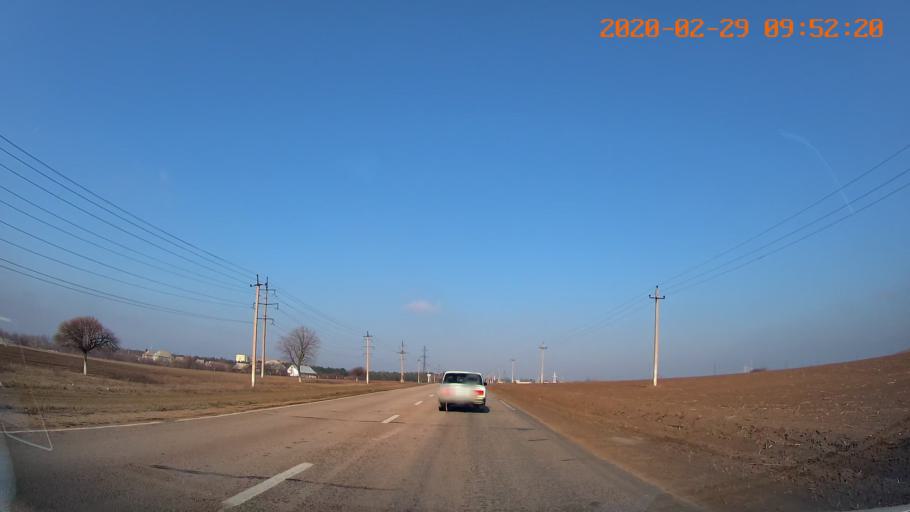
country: MD
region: Telenesti
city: Slobozia
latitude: 46.7153
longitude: 29.7317
